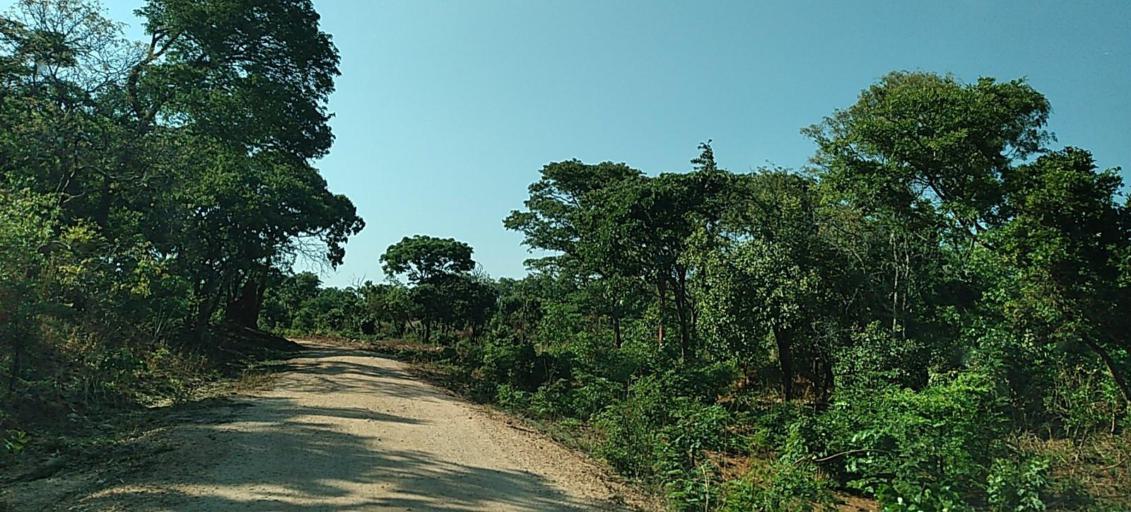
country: ZM
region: Central
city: Mkushi
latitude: -13.4658
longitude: 28.9144
